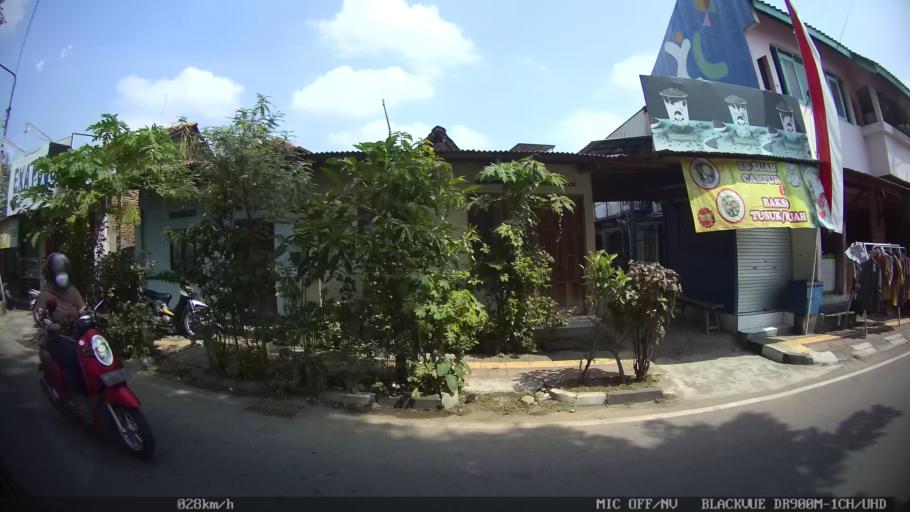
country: ID
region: Daerah Istimewa Yogyakarta
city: Yogyakarta
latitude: -7.8053
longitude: 110.3884
